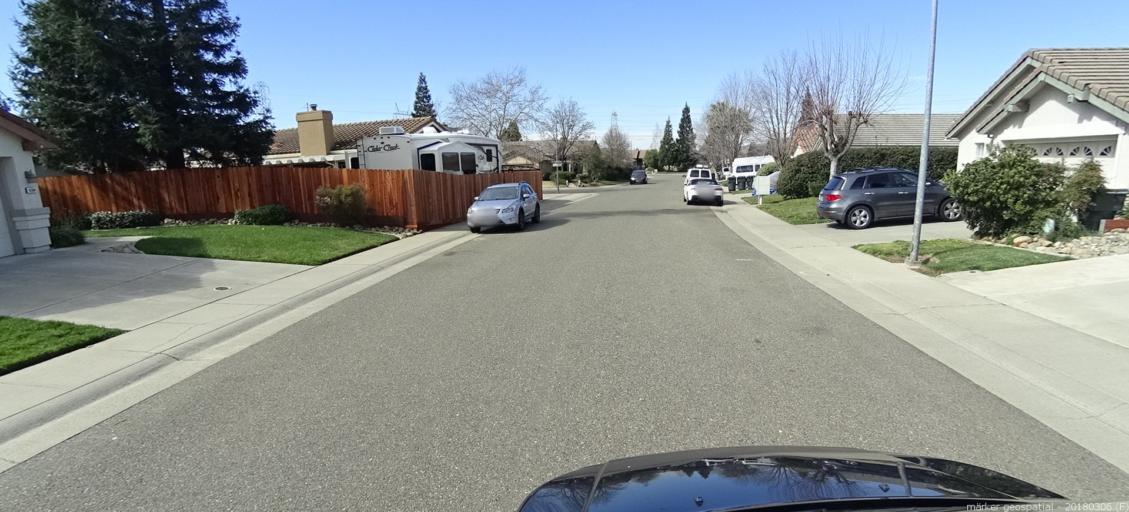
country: US
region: California
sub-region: Sacramento County
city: Vineyard
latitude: 38.4646
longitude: -121.3490
